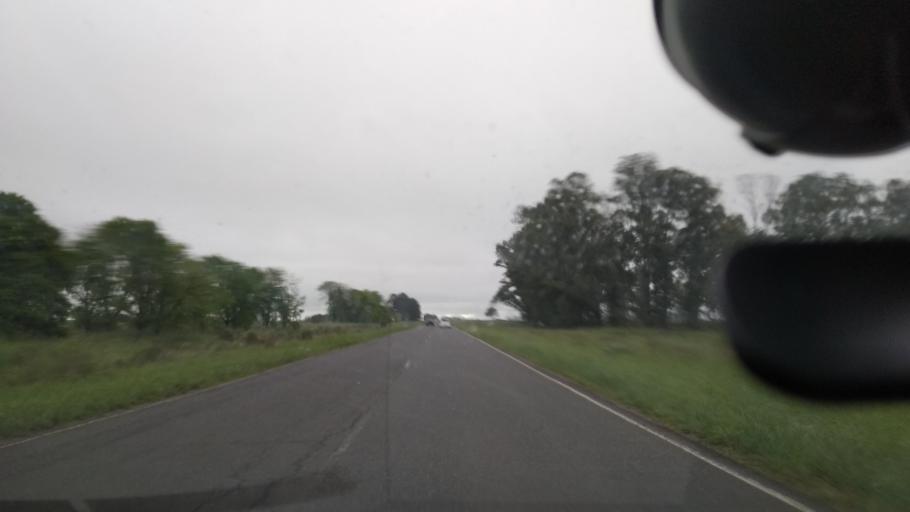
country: AR
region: Buenos Aires
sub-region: Partido de Magdalena
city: Magdalena
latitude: -35.2107
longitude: -57.7558
